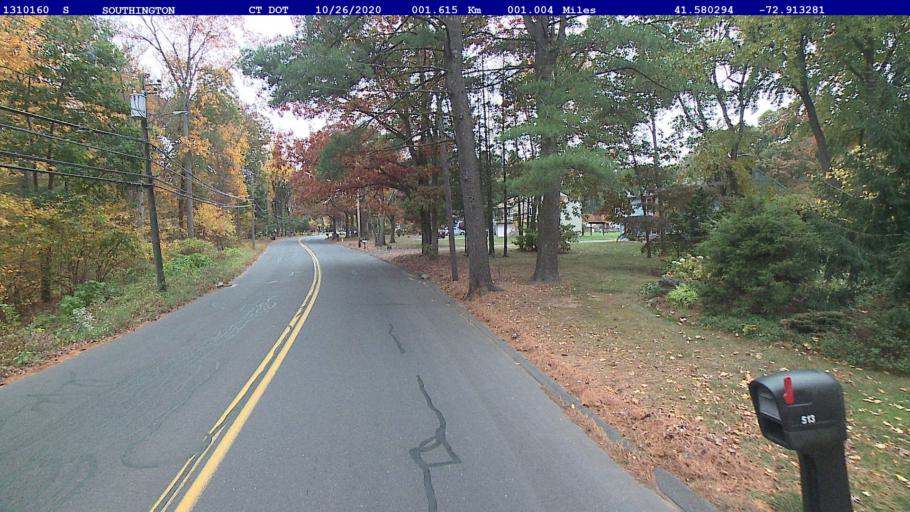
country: US
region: Connecticut
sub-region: New Haven County
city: Wolcott
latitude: 41.5803
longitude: -72.9133
